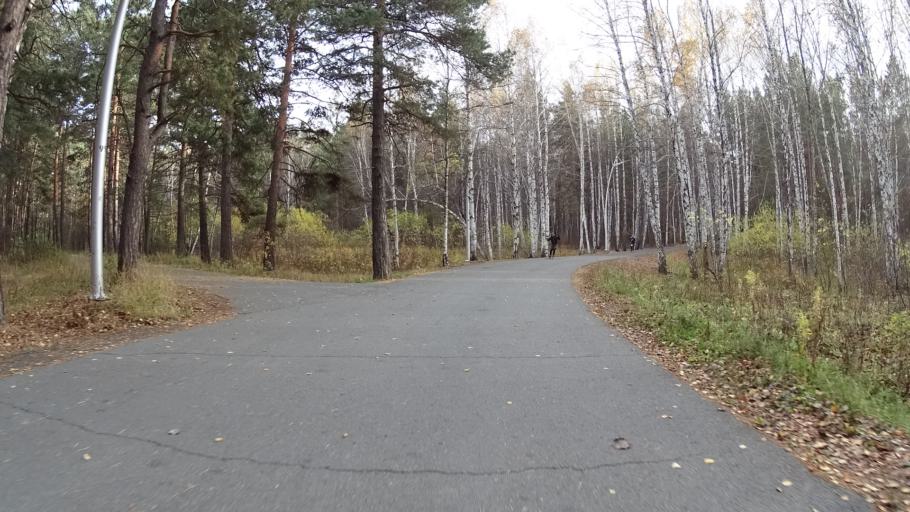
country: RU
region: Chelyabinsk
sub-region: Gorod Chelyabinsk
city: Chelyabinsk
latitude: 55.1395
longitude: 61.3511
